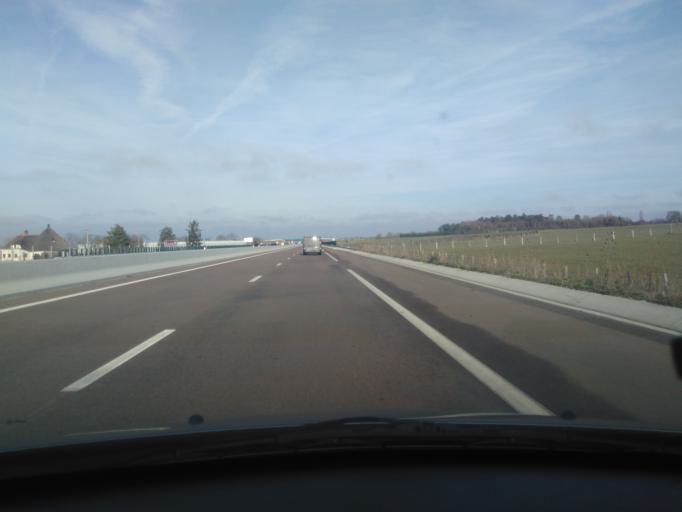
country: FR
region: Bourgogne
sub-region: Departement de la Nievre
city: Saint-Pierre-le-Moutier
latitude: 46.8107
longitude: 3.1224
